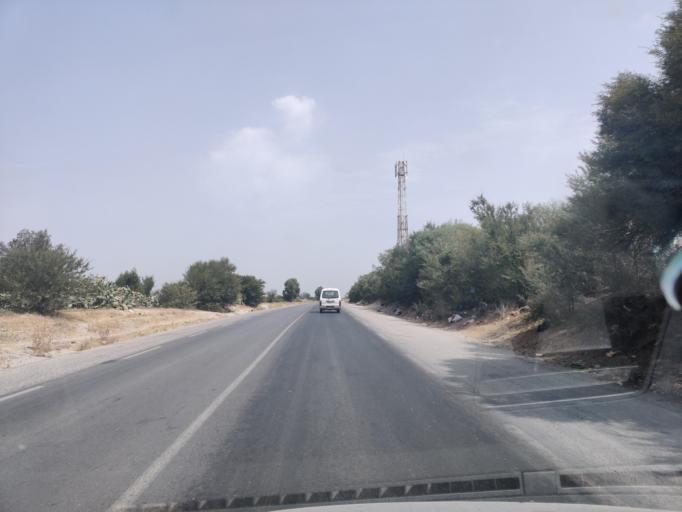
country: TN
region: Nabul
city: Bu `Urqub
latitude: 36.4803
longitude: 10.5718
